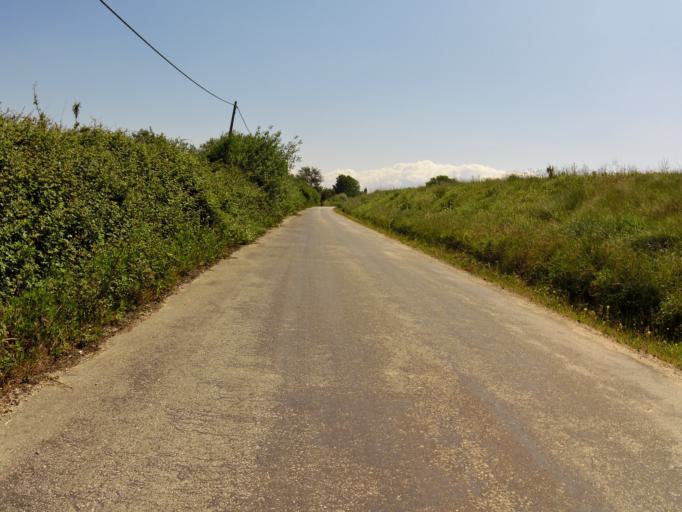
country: PT
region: Coimbra
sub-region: Montemor-O-Velho
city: Montemor-o-Velho
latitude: 40.1493
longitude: -8.7220
